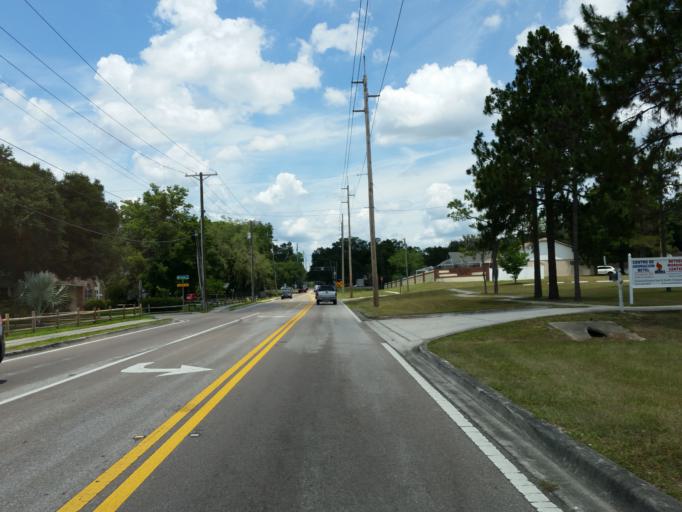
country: US
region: Florida
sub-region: Hillsborough County
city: Valrico
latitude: 27.9456
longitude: -82.2528
